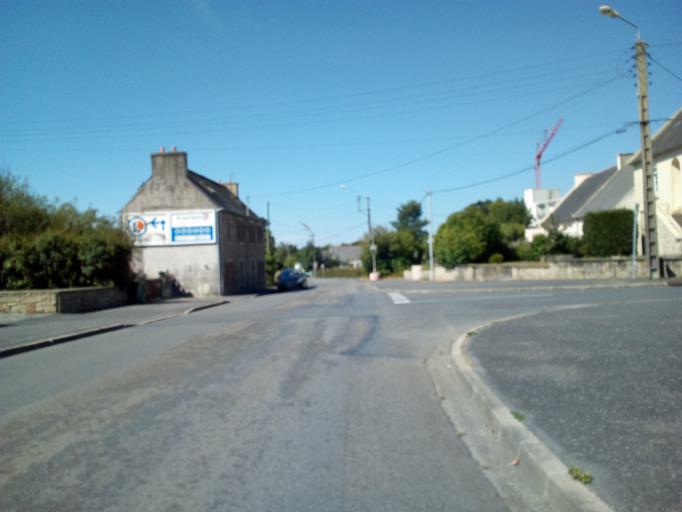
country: FR
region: Brittany
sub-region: Departement du Finistere
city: Landivisiau
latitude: 48.5037
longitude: -4.0697
